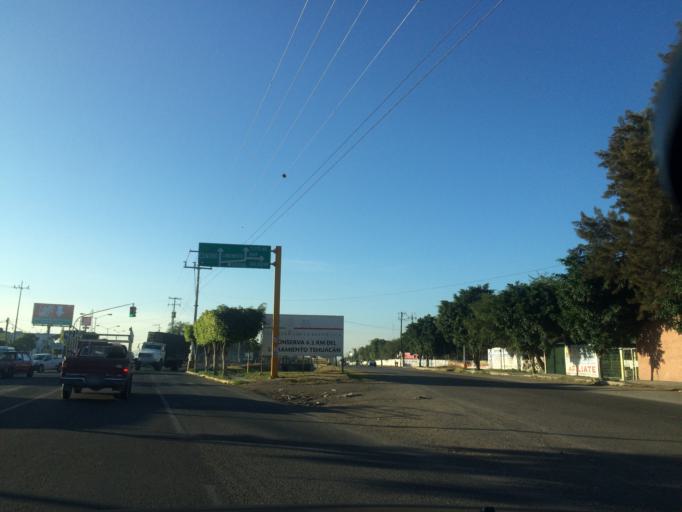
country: MX
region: Puebla
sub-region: Santiago Miahuatlan
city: San Jose Monte Chiquito
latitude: 18.4715
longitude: -97.4246
